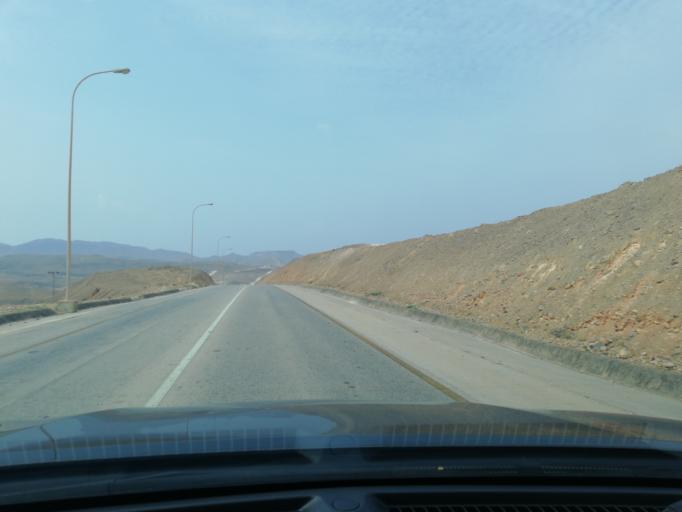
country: OM
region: Zufar
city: Salalah
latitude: 16.9274
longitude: 53.8427
